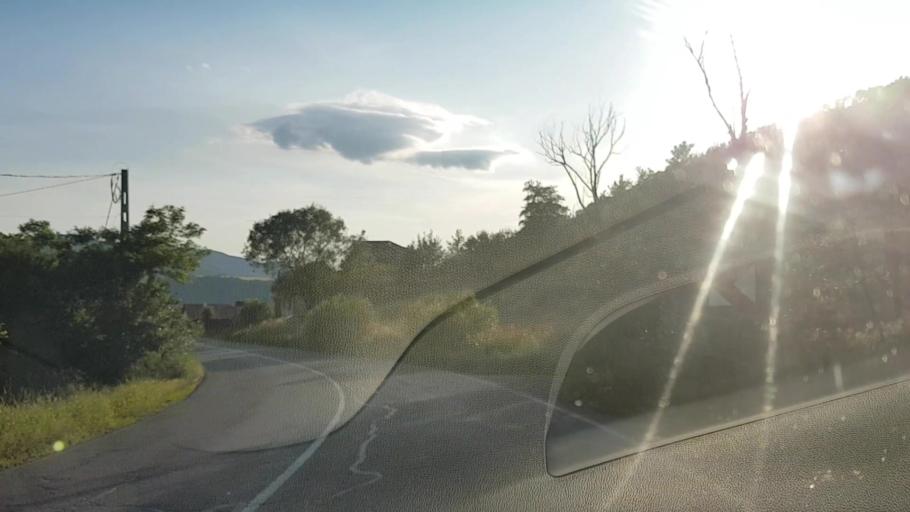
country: RO
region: Harghita
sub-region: Comuna Praid
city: Praid
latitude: 46.5643
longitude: 25.1552
